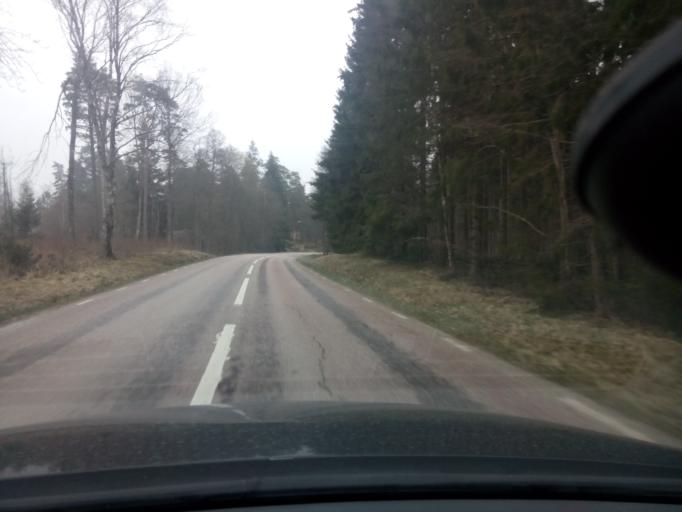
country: SE
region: Soedermanland
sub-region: Nykopings Kommun
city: Nykoping
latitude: 58.9309
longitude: 17.1090
